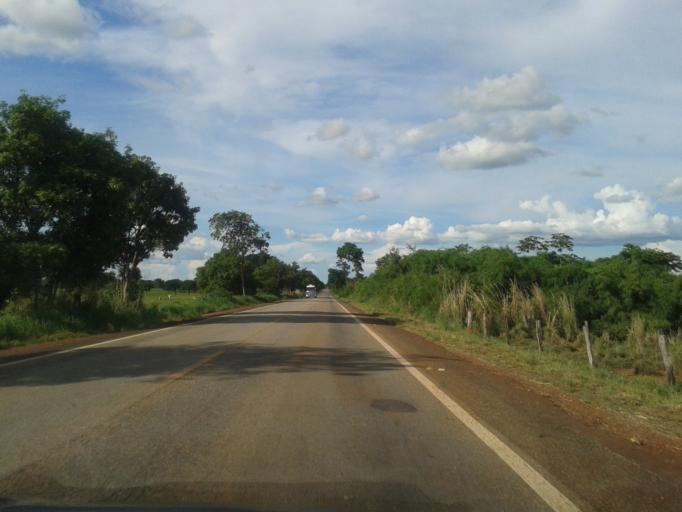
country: BR
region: Goias
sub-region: Mozarlandia
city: Mozarlandia
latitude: -14.2948
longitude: -50.4029
